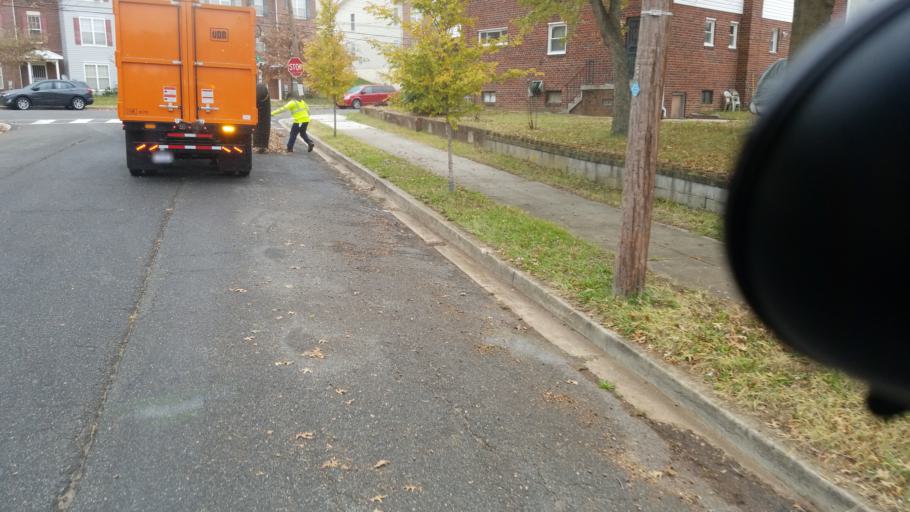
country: US
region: Maryland
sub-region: Prince George's County
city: Capitol Heights
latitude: 38.8874
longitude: -76.9206
